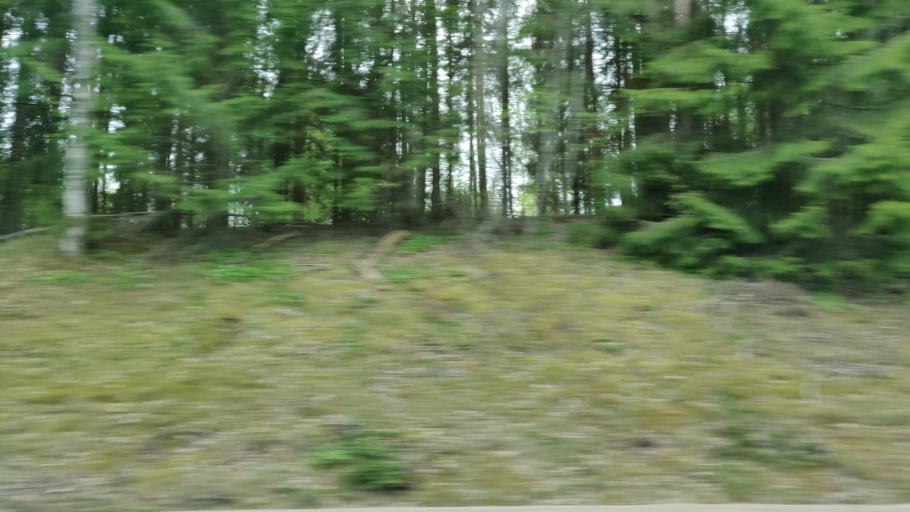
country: SE
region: Vaermland
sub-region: Forshaga Kommun
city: Deje
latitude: 59.6504
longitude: 13.4411
